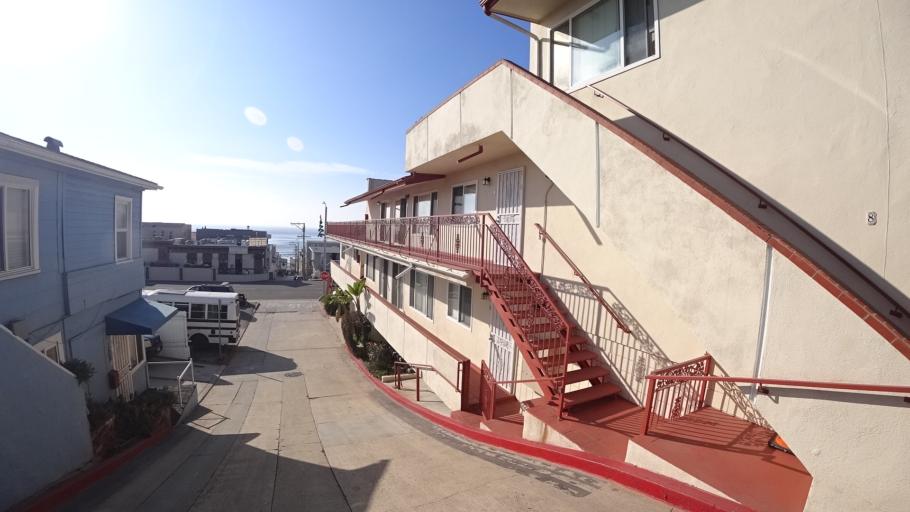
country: US
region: California
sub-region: Los Angeles County
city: El Segundo
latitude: 33.9020
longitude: -118.4178
